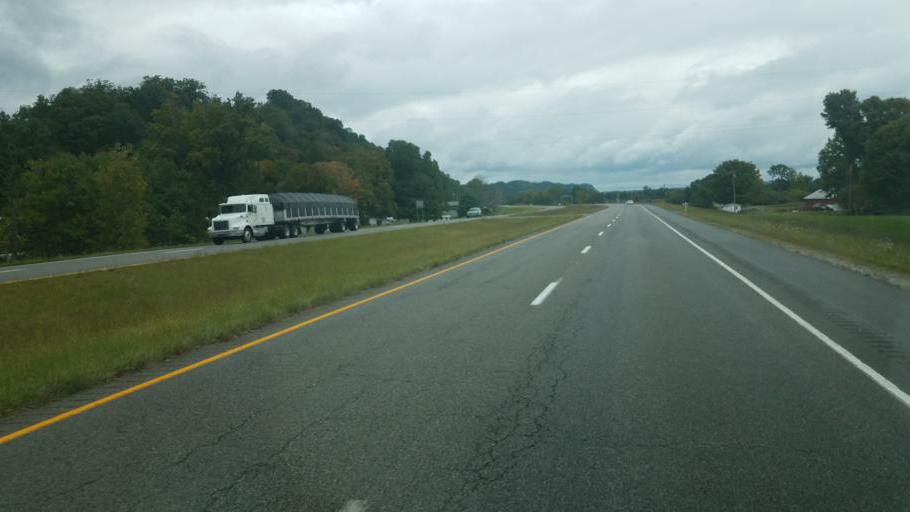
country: US
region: Ohio
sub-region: Scioto County
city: Franklin Furnace
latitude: 38.6635
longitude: -82.8784
